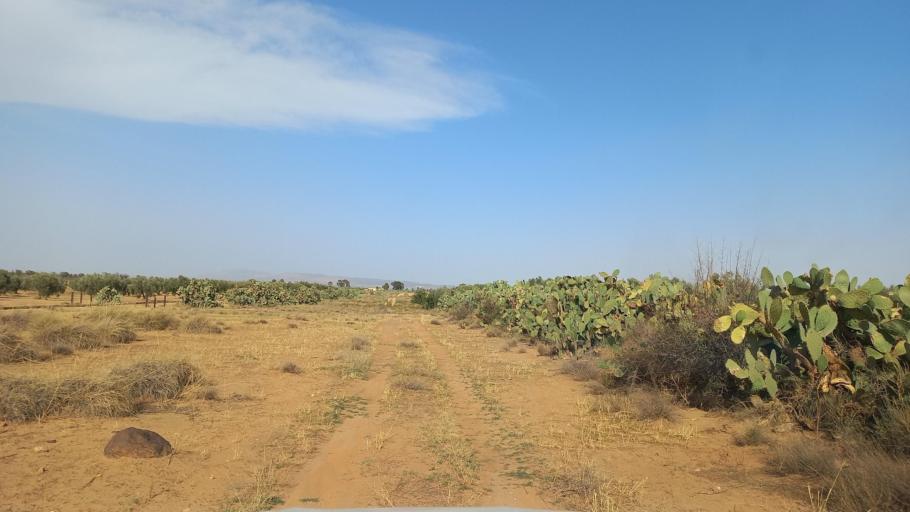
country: TN
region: Al Qasrayn
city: Kasserine
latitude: 35.2216
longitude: 8.9602
